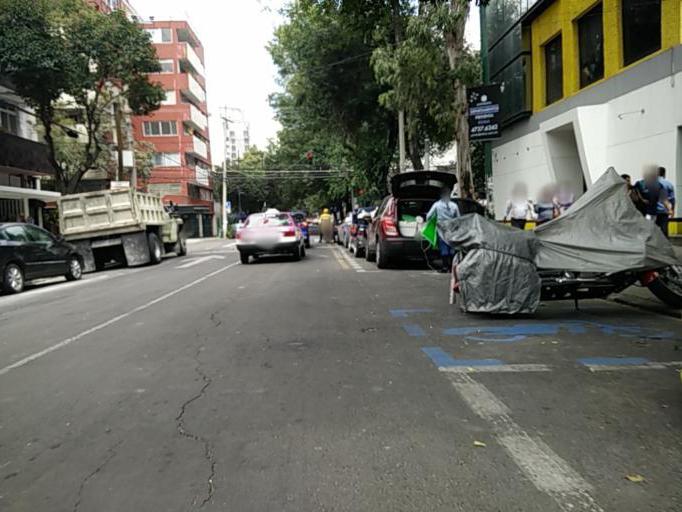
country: MX
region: Mexico City
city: Benito Juarez
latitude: 19.4193
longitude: -99.1613
